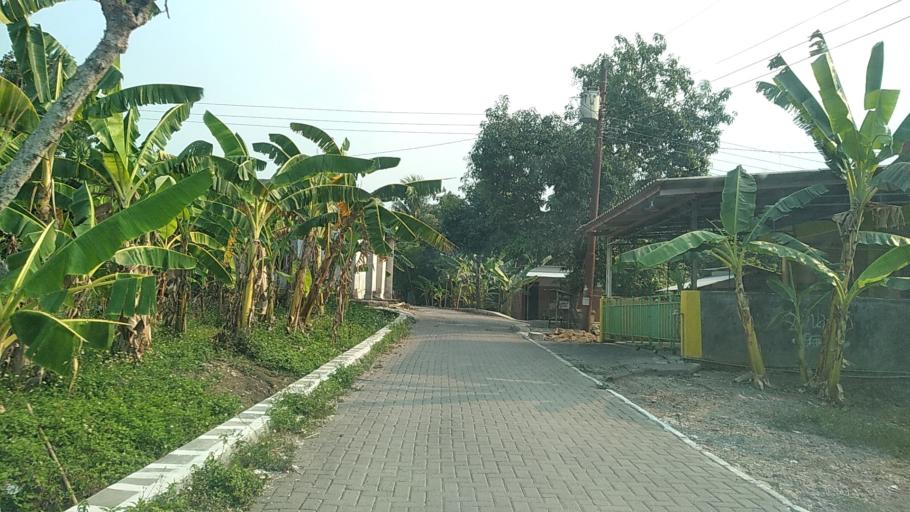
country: ID
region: Central Java
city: Mranggen
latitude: -7.0752
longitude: 110.4744
